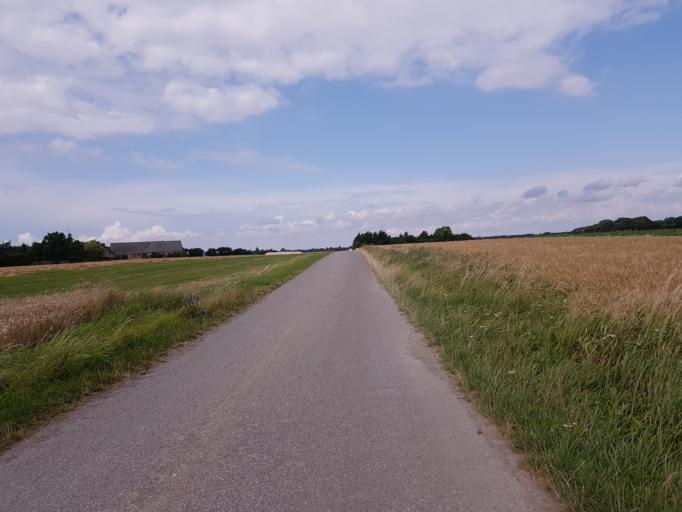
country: DK
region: Zealand
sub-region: Guldborgsund Kommune
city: Nykobing Falster
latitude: 54.5858
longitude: 11.9564
